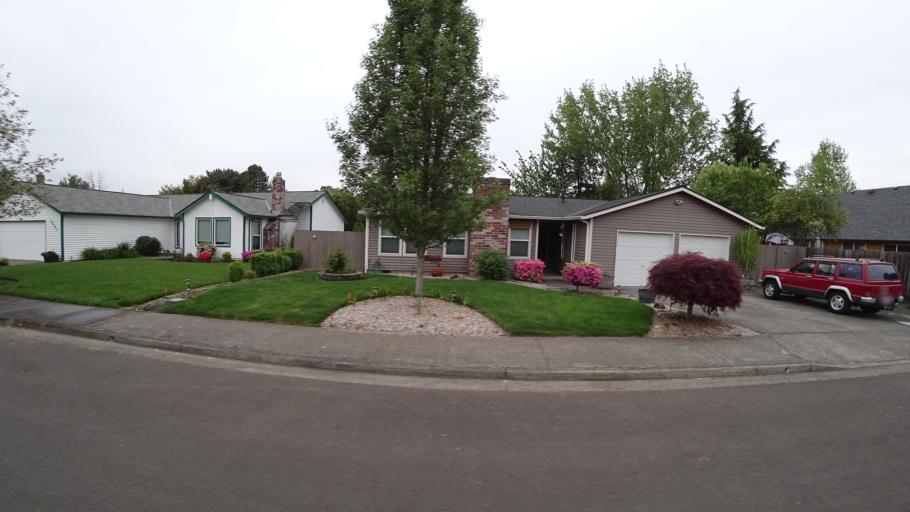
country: US
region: Oregon
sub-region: Washington County
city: Aloha
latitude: 45.5020
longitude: -122.8790
